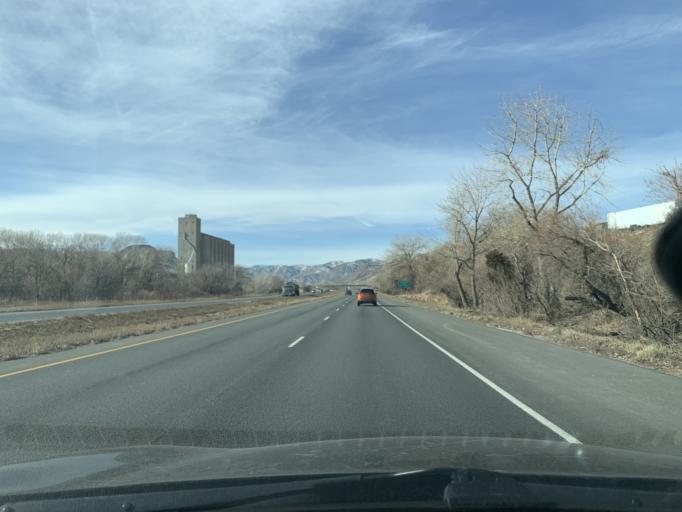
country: US
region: Colorado
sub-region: Jefferson County
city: Applewood
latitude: 39.7741
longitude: -105.1662
